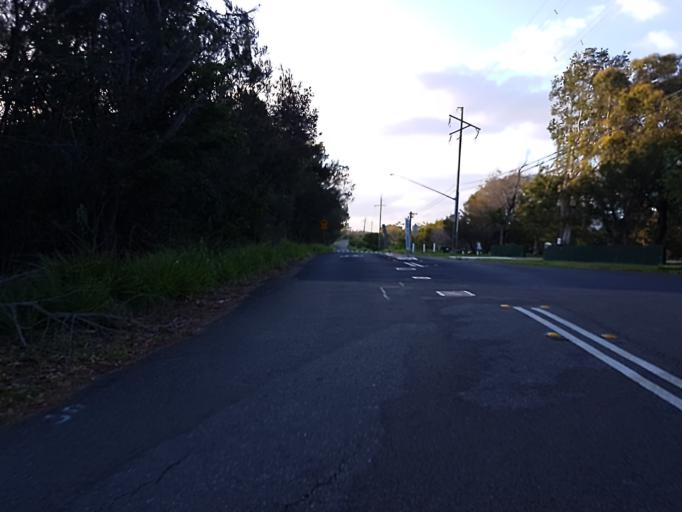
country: AU
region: New South Wales
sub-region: Warringah
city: Killarney Heights
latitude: -33.7617
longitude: 151.2311
